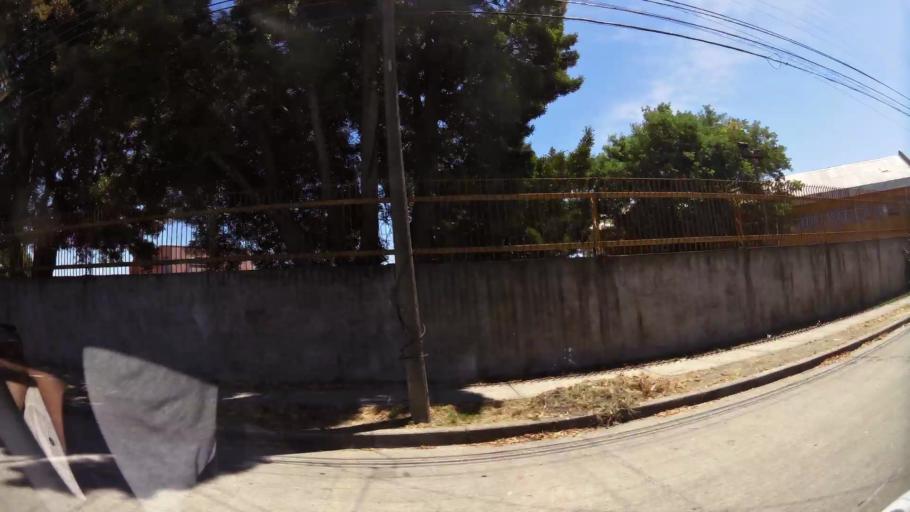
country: CL
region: Biobio
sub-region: Provincia de Concepcion
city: Talcahuano
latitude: -36.7473
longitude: -73.0903
